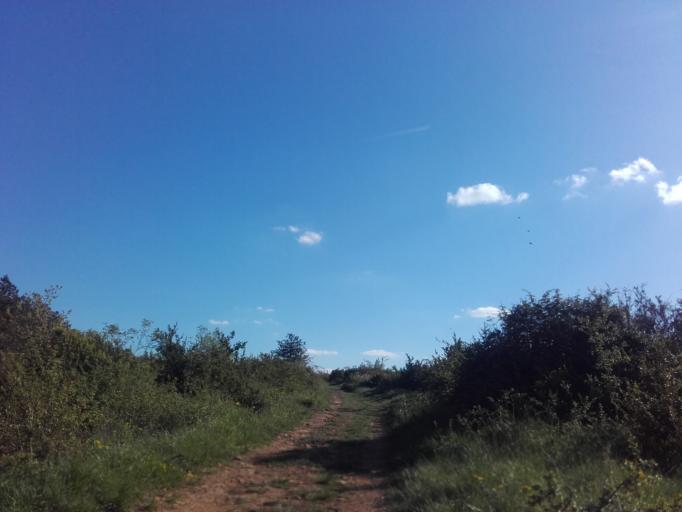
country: FR
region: Bourgogne
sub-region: Departement de Saone-et-Loire
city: Chagny
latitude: 46.8943
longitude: 4.7399
